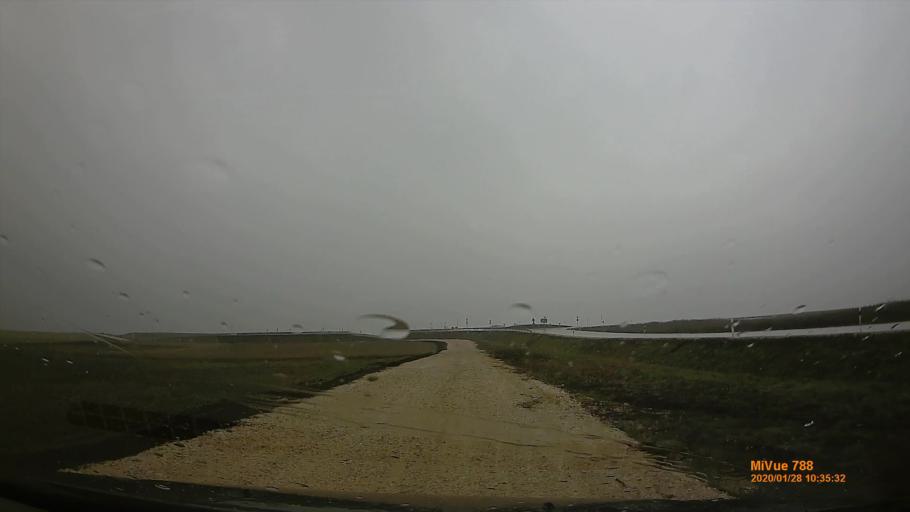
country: HU
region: Pest
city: Monor
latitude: 47.3607
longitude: 19.4889
